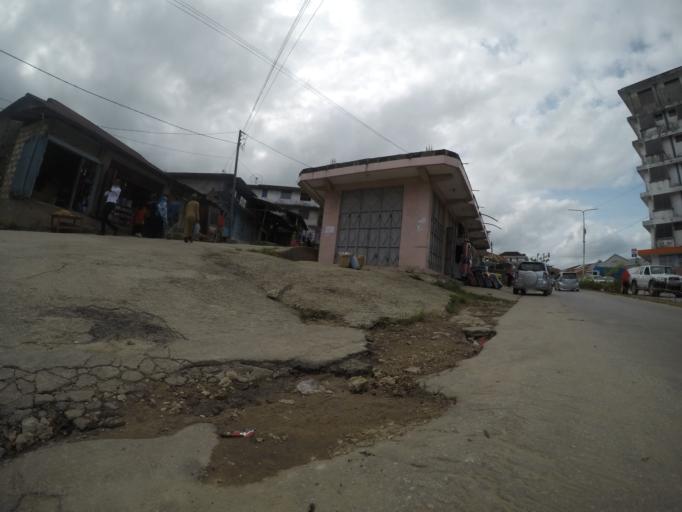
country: TZ
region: Pemba South
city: Chake Chake
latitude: -5.2471
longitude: 39.7694
